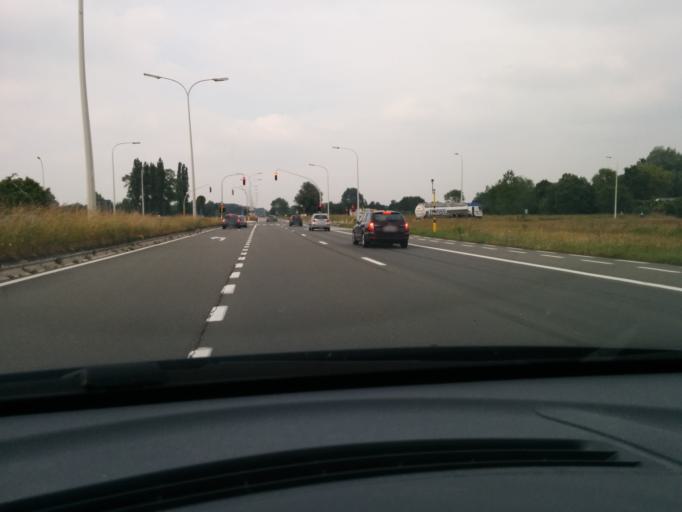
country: BE
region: Flanders
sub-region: Provincie Oost-Vlaanderen
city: De Pinte
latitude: 50.9859
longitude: 3.6741
